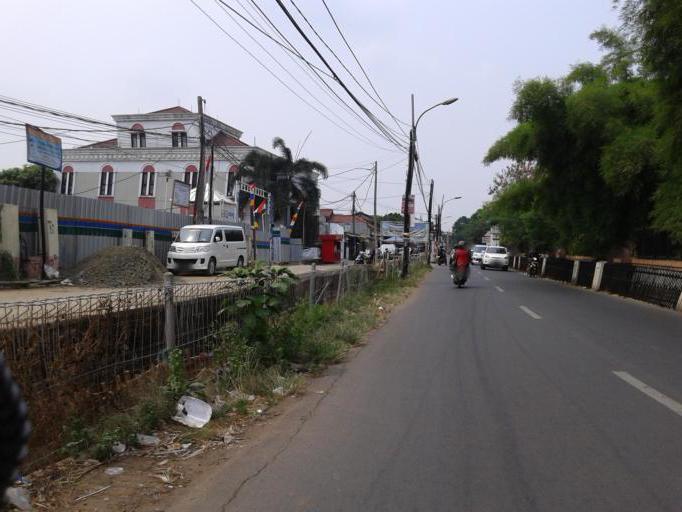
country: ID
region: West Java
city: Pamulang
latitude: -6.3128
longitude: 106.7588
